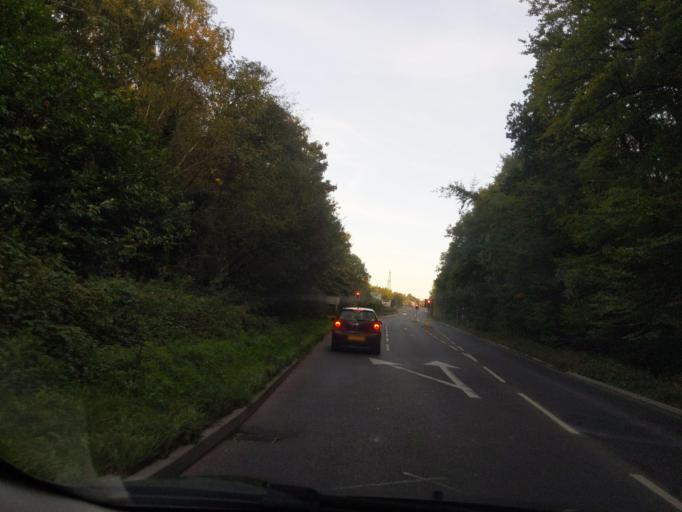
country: GB
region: England
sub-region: Devon
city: Bovey Tracey
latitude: 50.5696
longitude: -3.6587
